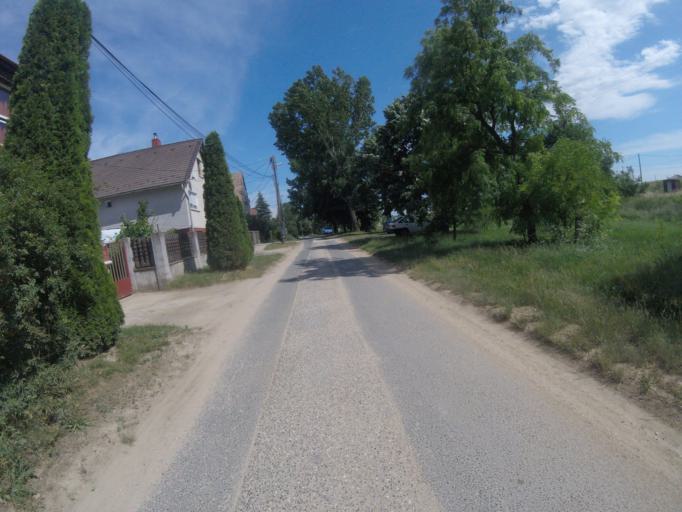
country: HU
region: Fejer
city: Szarliget
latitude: 47.4834
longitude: 18.5040
